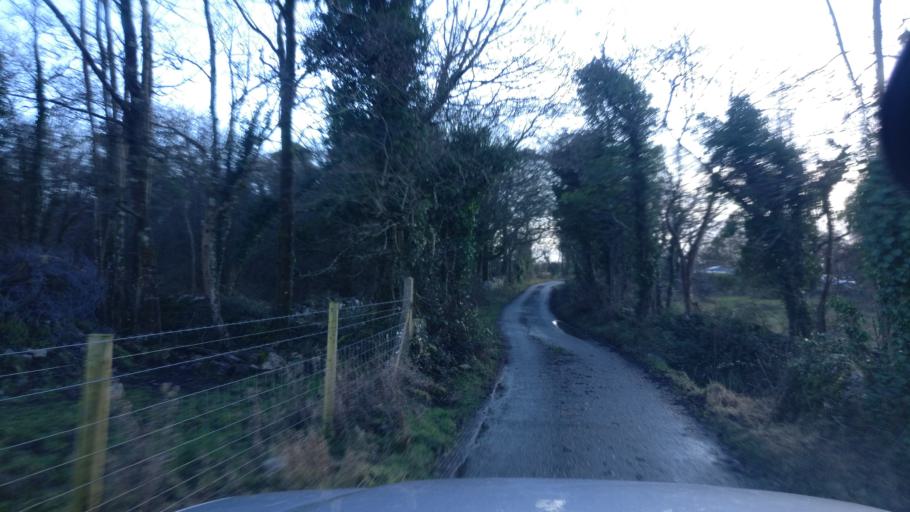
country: IE
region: Connaught
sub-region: County Galway
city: Loughrea
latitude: 53.2405
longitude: -8.5768
